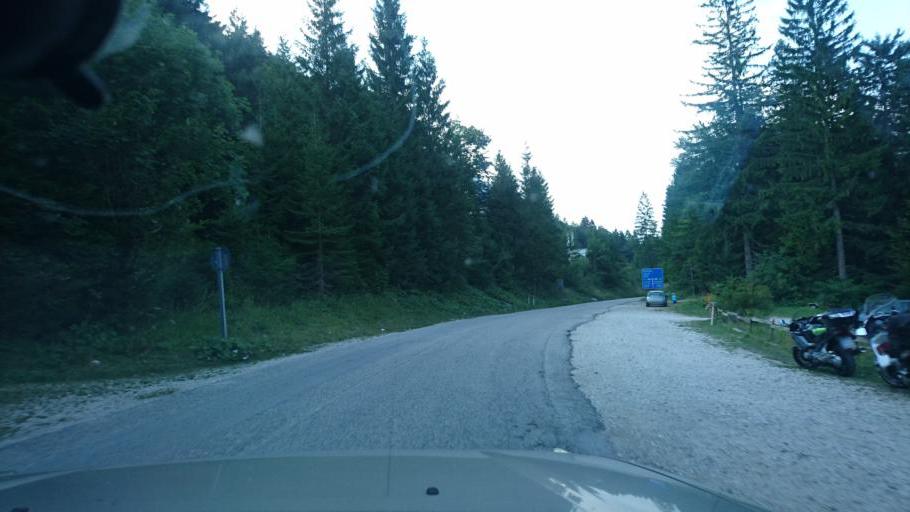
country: IT
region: Friuli Venezia Giulia
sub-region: Provincia di Udine
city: Tarvisio
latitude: 46.4258
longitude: 13.5652
